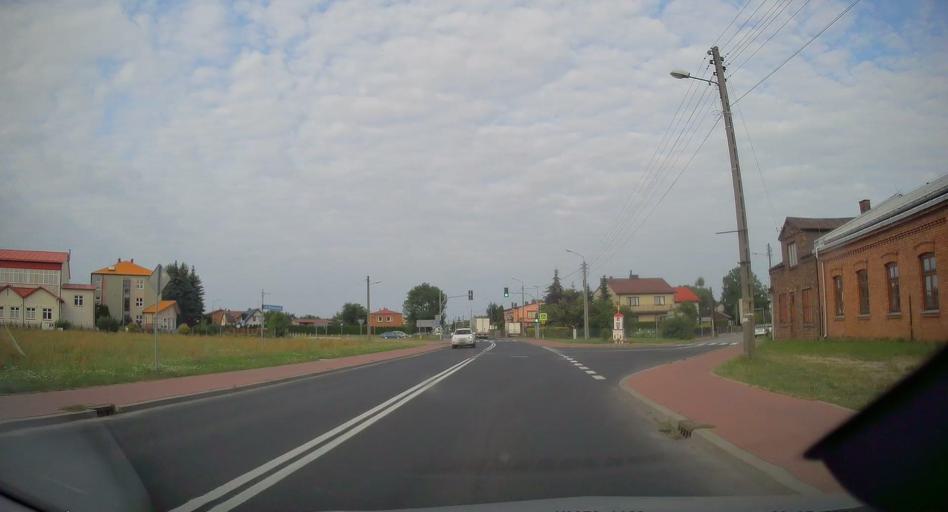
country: PL
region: Silesian Voivodeship
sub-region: Powiat czestochowski
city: Klomnice
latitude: 50.9227
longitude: 19.3601
